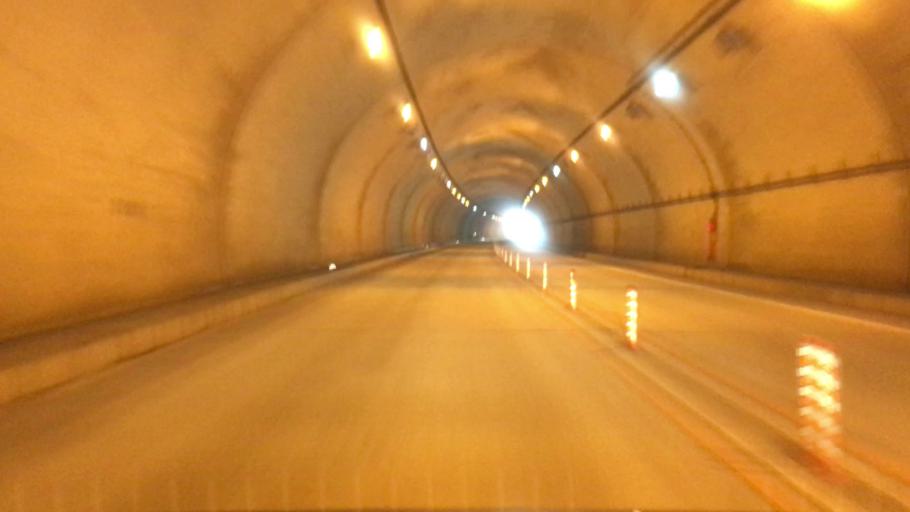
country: JP
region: Hyogo
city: Toyooka
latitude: 35.6285
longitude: 134.6055
